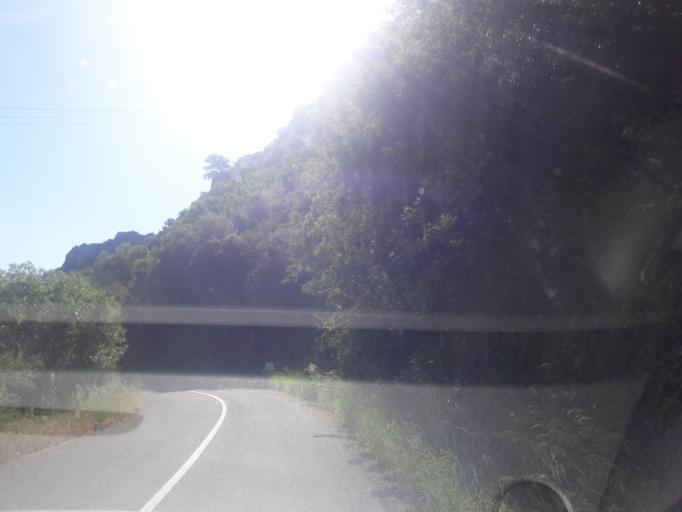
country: ES
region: Castille and Leon
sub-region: Provincia de Salamanca
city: Saucelle
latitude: 41.0228
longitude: -6.7464
